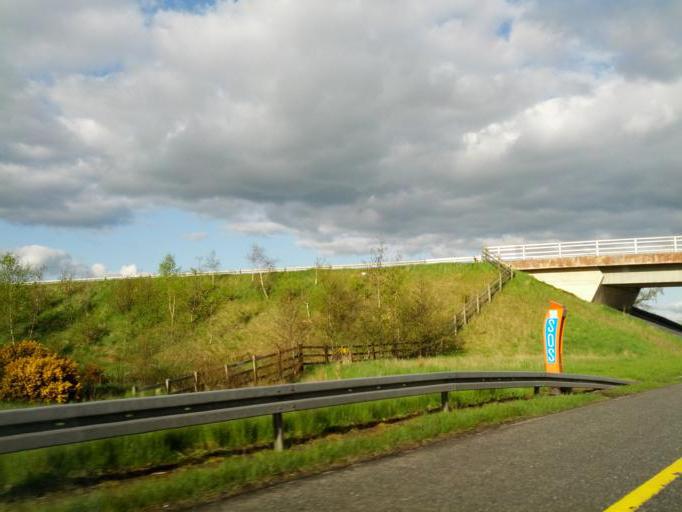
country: IE
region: Leinster
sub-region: An Mhi
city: Longwood
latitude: 53.4260
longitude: -6.9284
